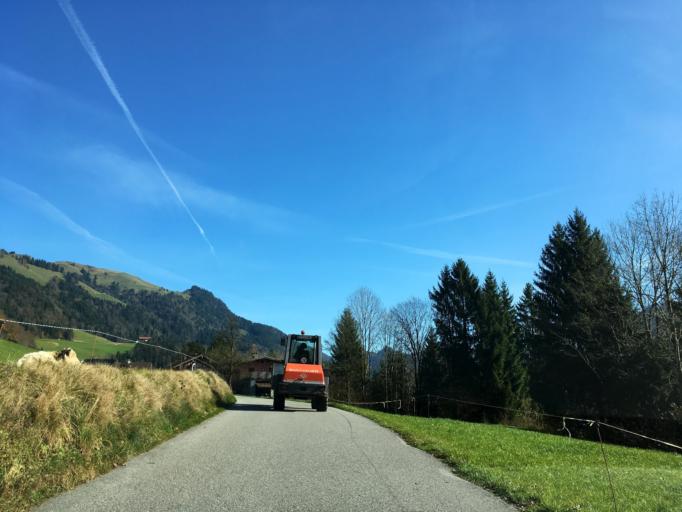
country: AT
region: Tyrol
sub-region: Politischer Bezirk Kufstein
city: Rettenschoss
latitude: 47.6582
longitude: 12.2761
